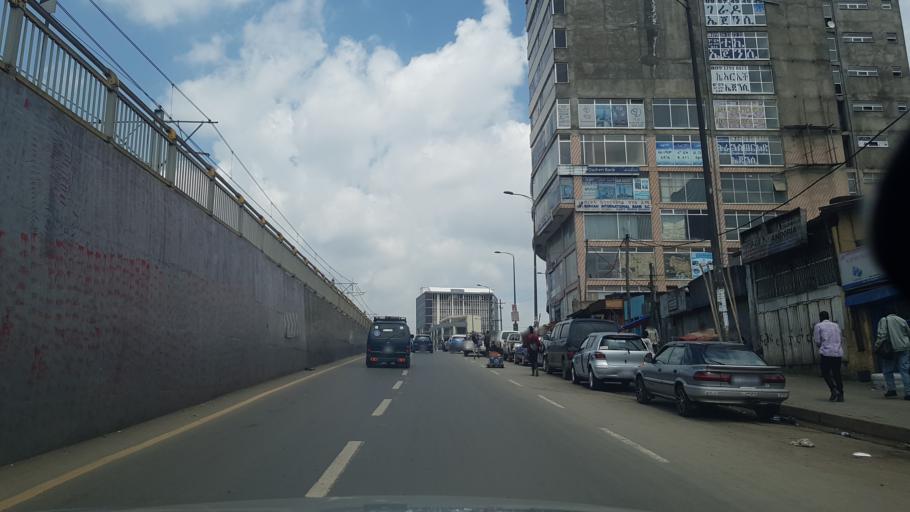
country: ET
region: Adis Abeba
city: Addis Ababa
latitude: 9.0344
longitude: 38.7450
